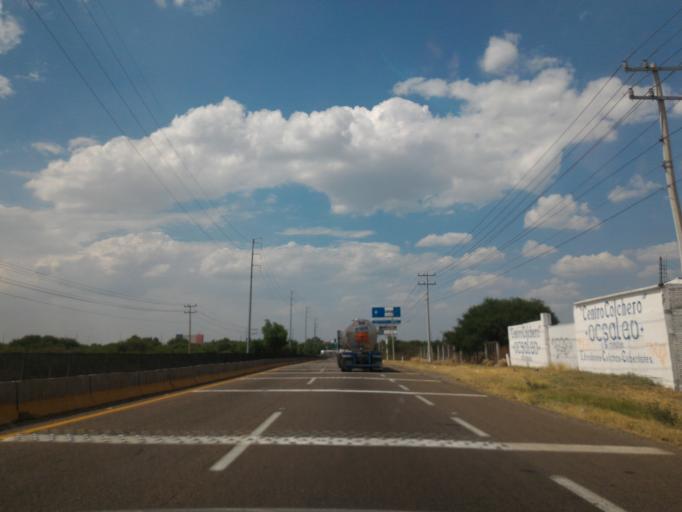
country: MX
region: Aguascalientes
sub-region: Aguascalientes
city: Penuelas (El Cienegal)
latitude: 21.7137
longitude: -102.2782
